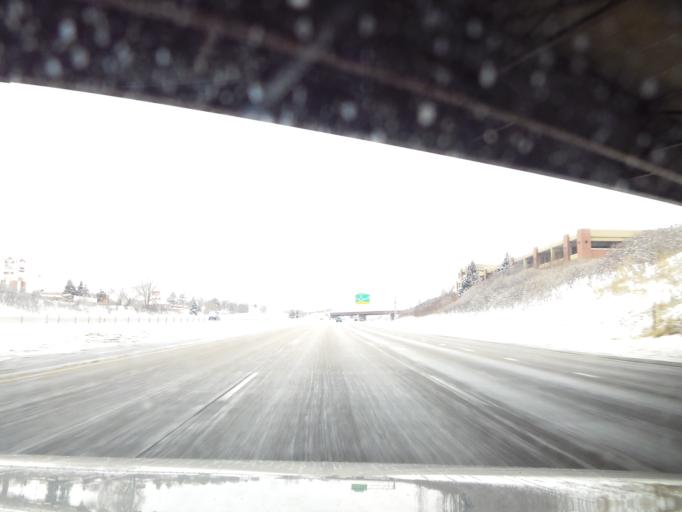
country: US
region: Minnesota
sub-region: Dakota County
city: Eagan
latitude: 44.8335
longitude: -93.1642
